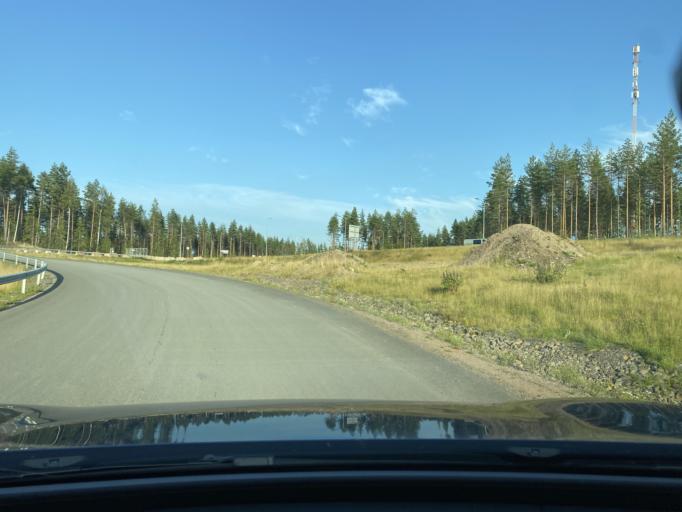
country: FI
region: Kymenlaakso
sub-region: Kouvola
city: Elimaeki
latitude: 60.8749
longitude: 26.4995
